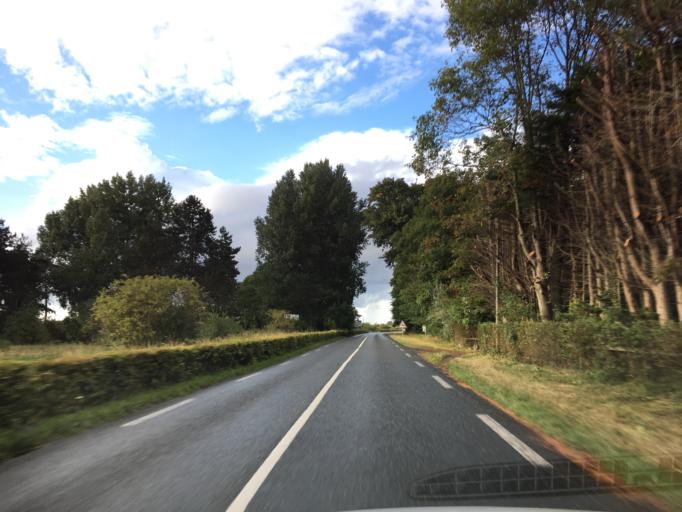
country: FR
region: Lower Normandy
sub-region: Departement du Calvados
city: Amfreville
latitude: 49.2681
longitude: -0.2206
